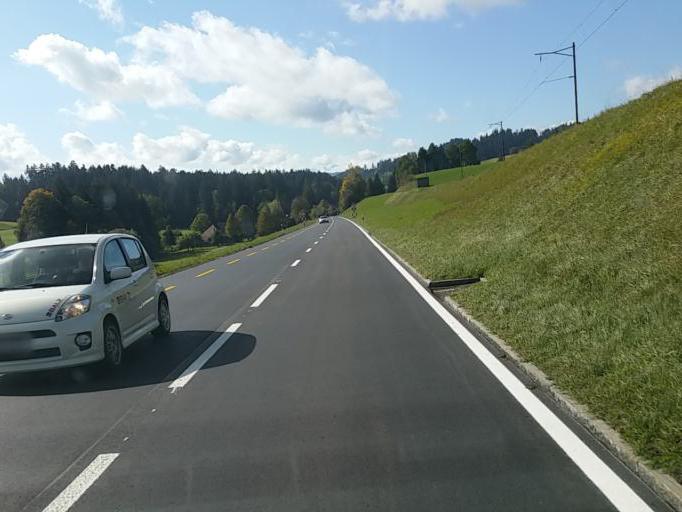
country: CH
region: Bern
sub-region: Emmental District
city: Sumiswald
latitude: 47.0492
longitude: 7.7477
